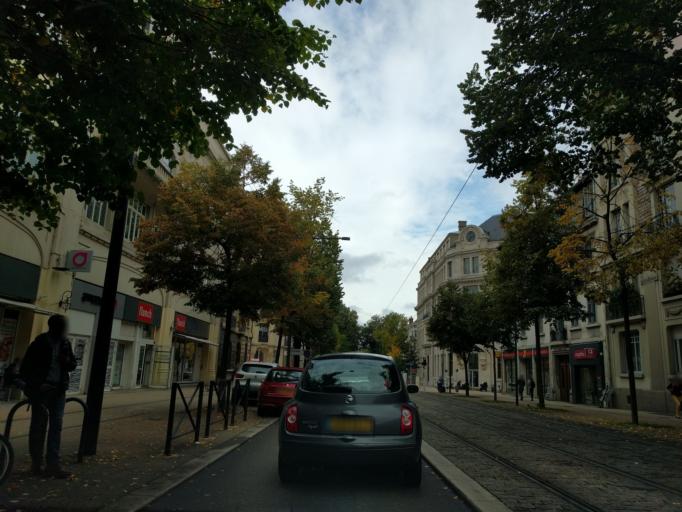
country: FR
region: Bourgogne
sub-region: Departement de la Cote-d'Or
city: Dijon
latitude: 47.3241
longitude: 5.0351
